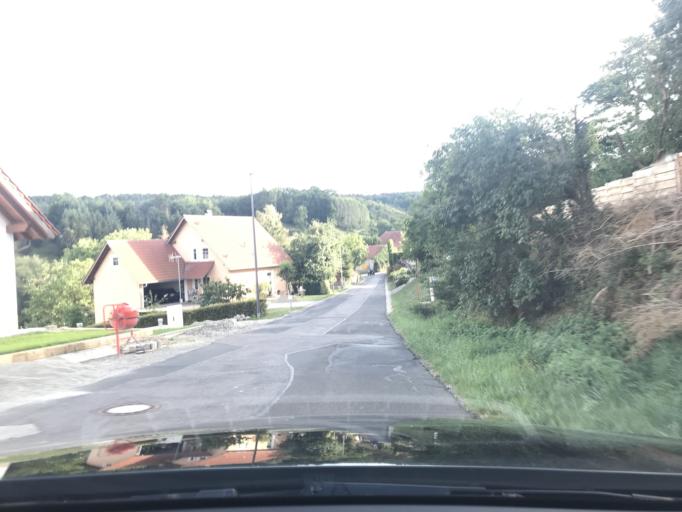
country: DE
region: Bavaria
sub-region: Regierungsbezirk Unterfranken
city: Kirchlauter
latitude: 50.0793
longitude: 10.6946
